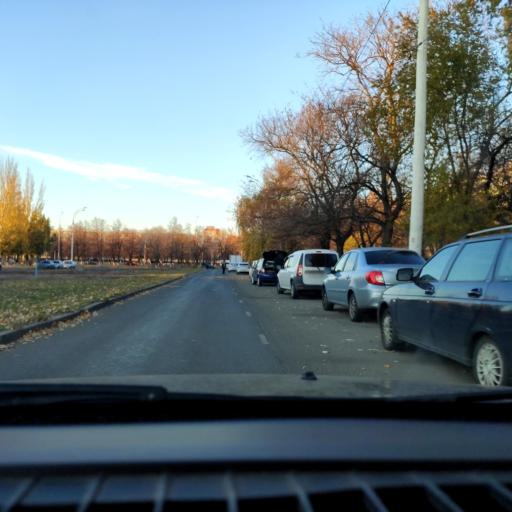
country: RU
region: Samara
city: Tol'yatti
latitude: 53.5174
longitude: 49.2861
